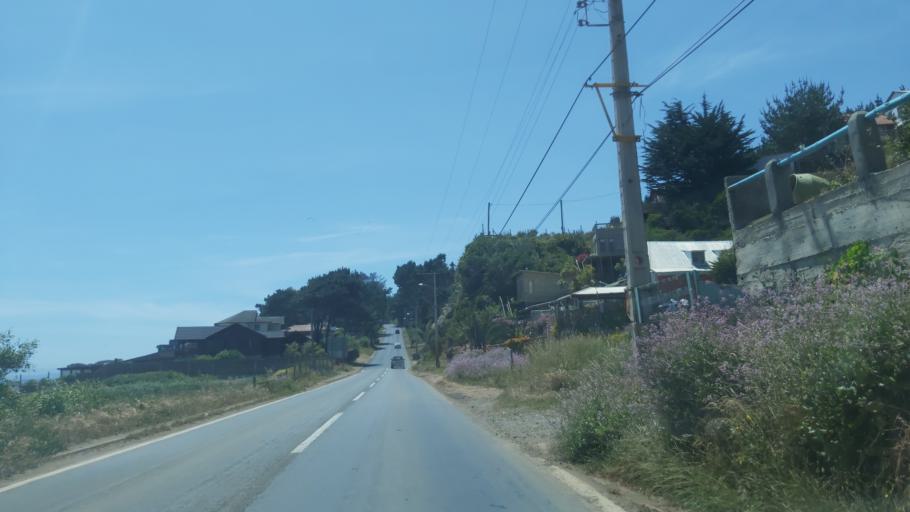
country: CL
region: Maule
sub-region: Provincia de Cauquenes
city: Cauquenes
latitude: -35.8362
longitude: -72.6238
